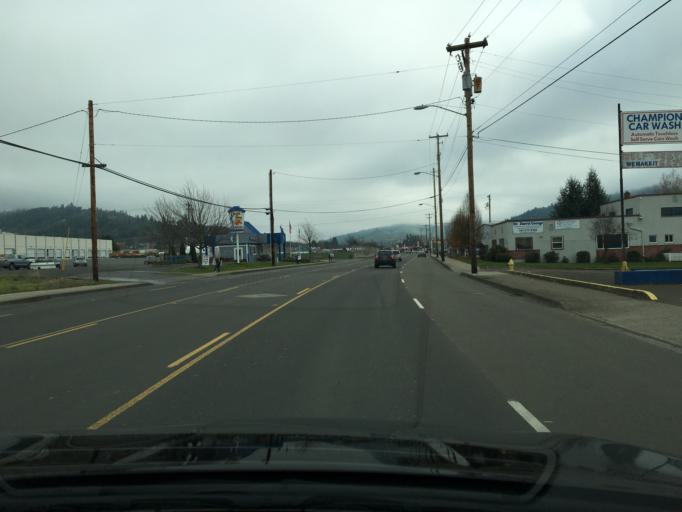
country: US
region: Oregon
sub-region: Douglas County
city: Roseburg
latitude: 43.2133
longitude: -123.3337
